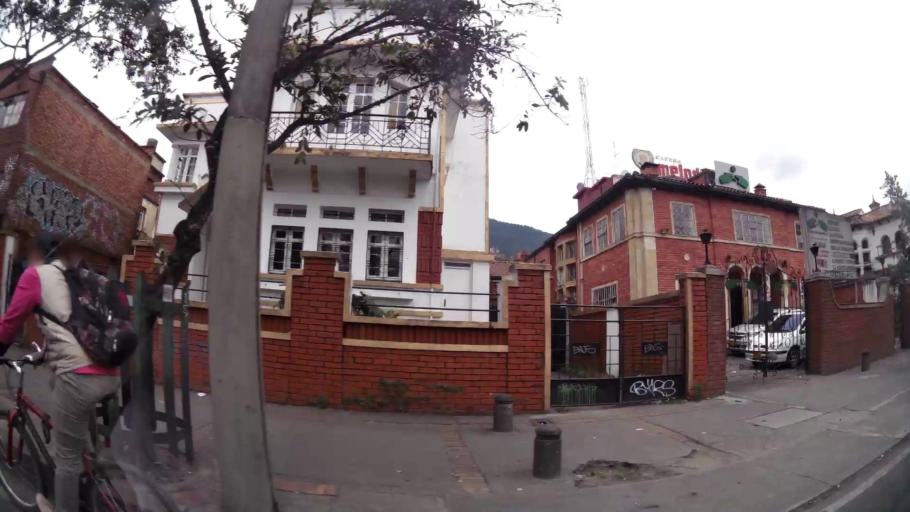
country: CO
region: Bogota D.C.
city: Bogota
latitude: 4.6330
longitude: -74.0675
